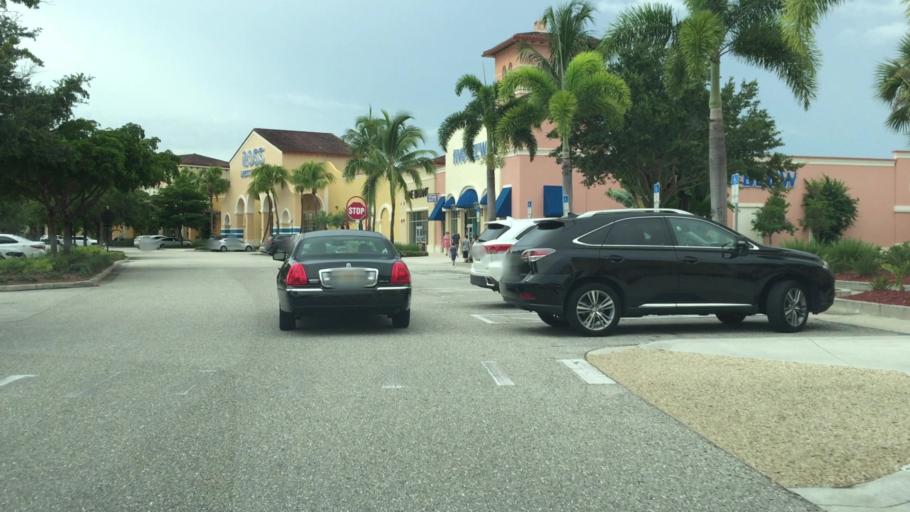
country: US
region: Florida
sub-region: Lee County
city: Estero
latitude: 26.4070
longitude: -81.8062
